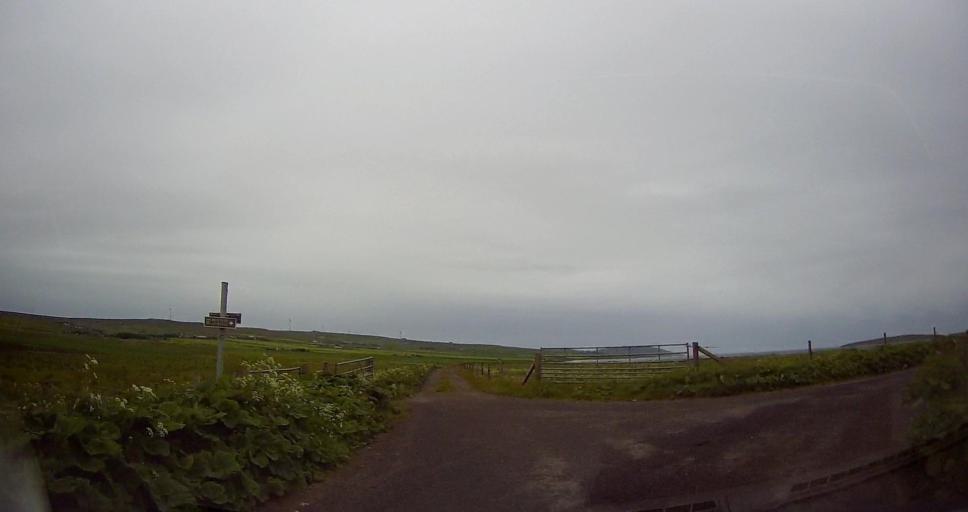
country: GB
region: Scotland
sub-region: Orkney Islands
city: Orkney
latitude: 59.1169
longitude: -3.0839
